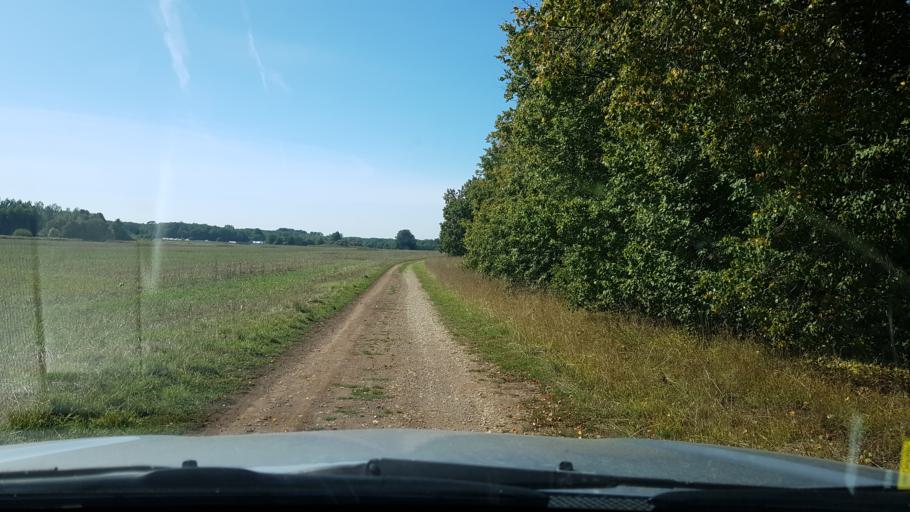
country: EE
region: Ida-Virumaa
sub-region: Sillamaee linn
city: Sillamae
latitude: 59.3946
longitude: 27.8452
